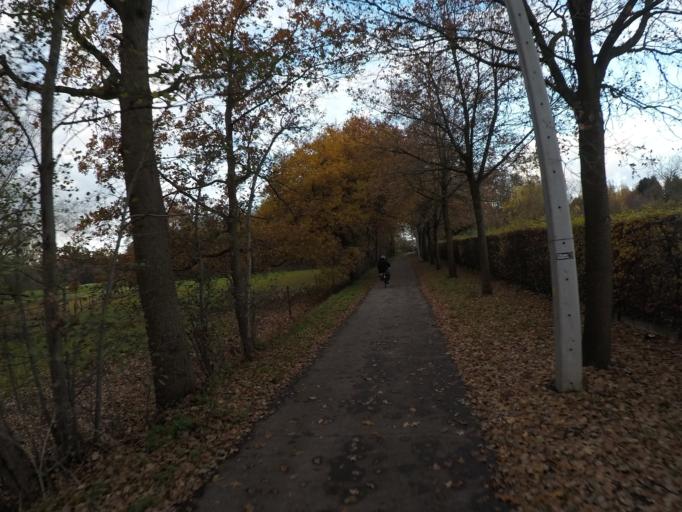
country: BE
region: Flanders
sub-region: Provincie Vlaams-Brabant
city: Londerzeel
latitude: 51.0056
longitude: 4.2948
